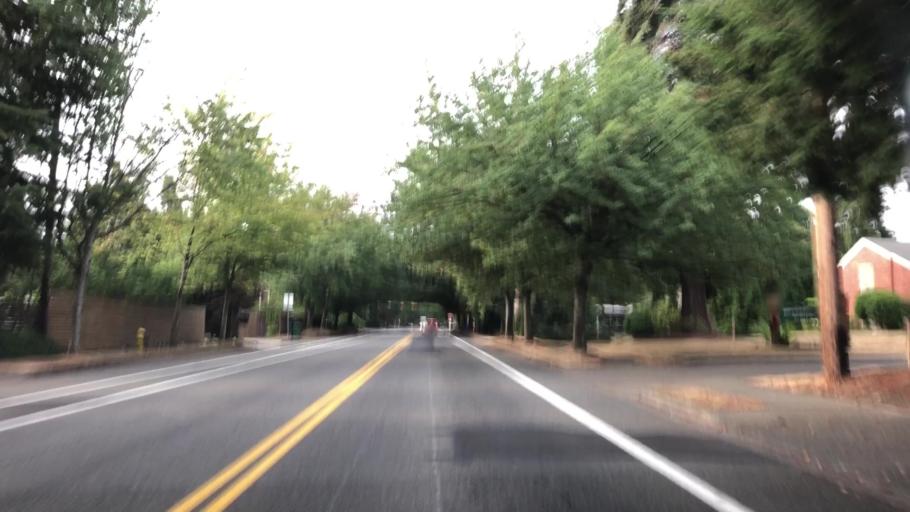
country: US
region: Washington
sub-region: King County
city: Redmond
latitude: 47.6770
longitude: -122.1639
